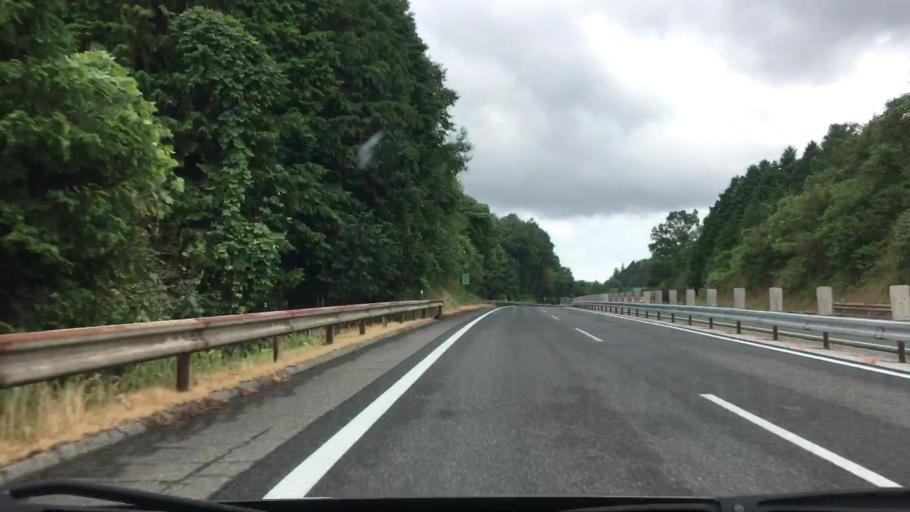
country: JP
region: Okayama
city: Niimi
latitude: 34.9147
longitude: 133.3133
